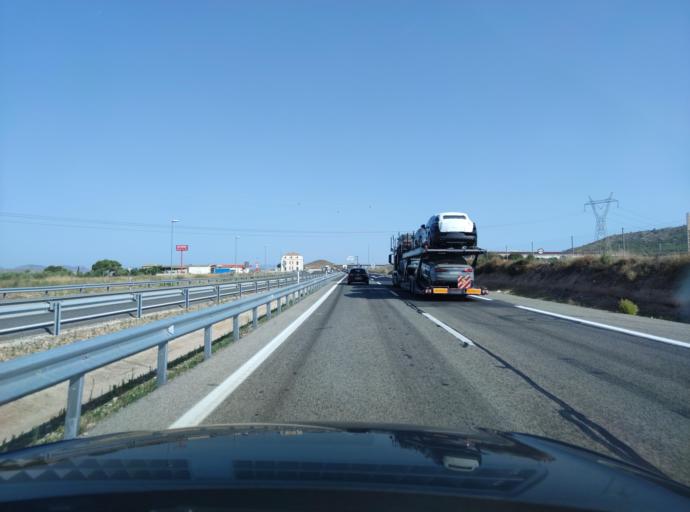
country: ES
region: Valencia
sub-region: Provincia de Alicante
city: Sax
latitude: 38.5705
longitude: -0.8370
